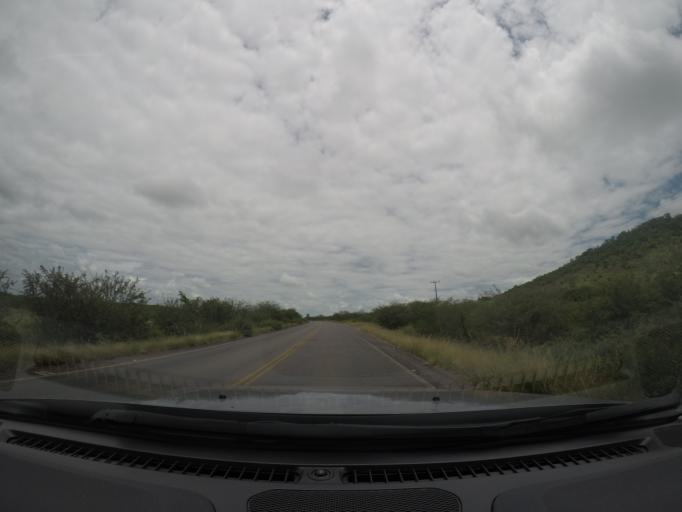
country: BR
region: Bahia
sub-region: Itaberaba
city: Itaberaba
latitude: -12.5006
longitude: -40.2453
